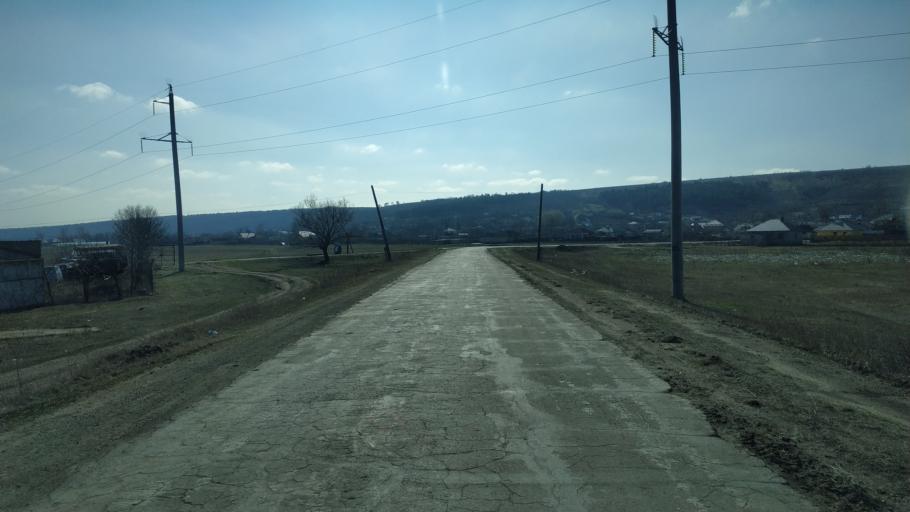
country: MD
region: Hincesti
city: Hincesti
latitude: 46.7521
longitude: 28.6517
